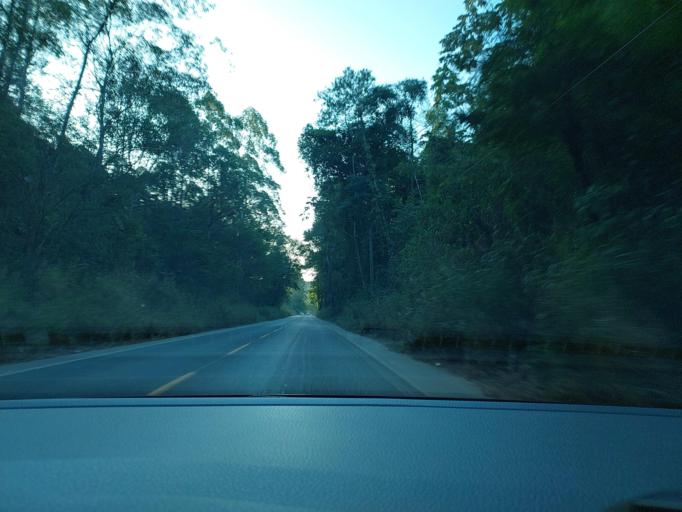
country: BR
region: Minas Gerais
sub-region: Vicosa
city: Vicosa
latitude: -20.8021
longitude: -42.8336
